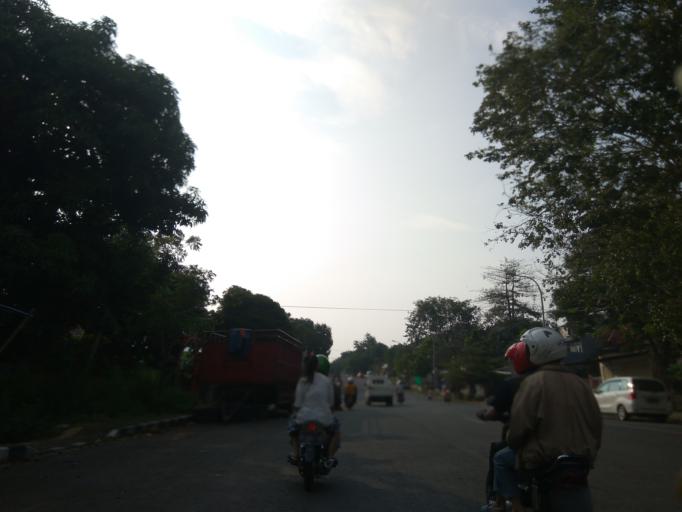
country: ID
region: Central Java
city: Semarang
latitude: -7.0014
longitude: 110.3913
